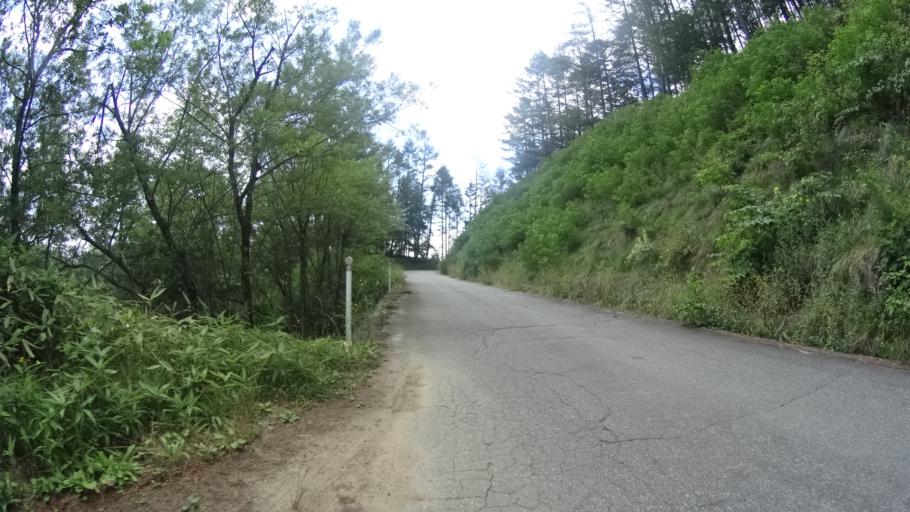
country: JP
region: Yamanashi
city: Enzan
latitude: 35.8268
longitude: 138.6445
